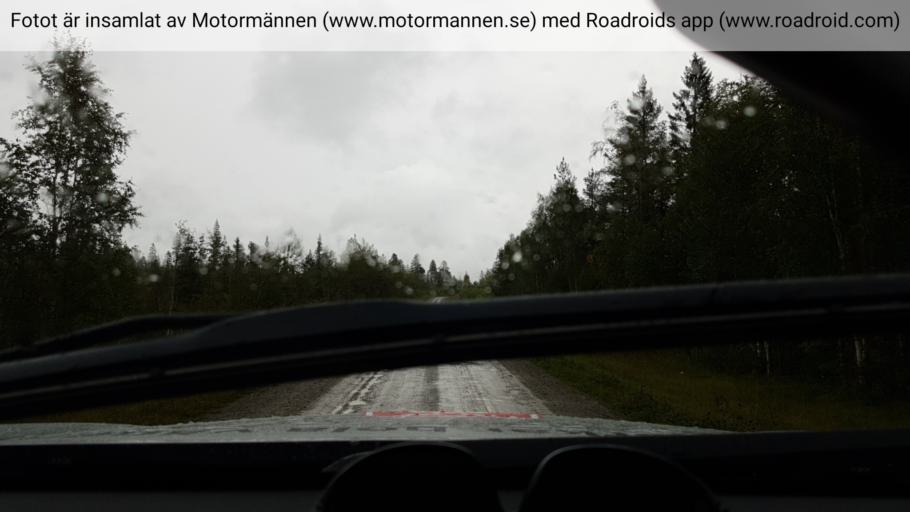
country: SE
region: Vaesterbotten
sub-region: Asele Kommun
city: Insjon
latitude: 64.7848
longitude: 17.5617
